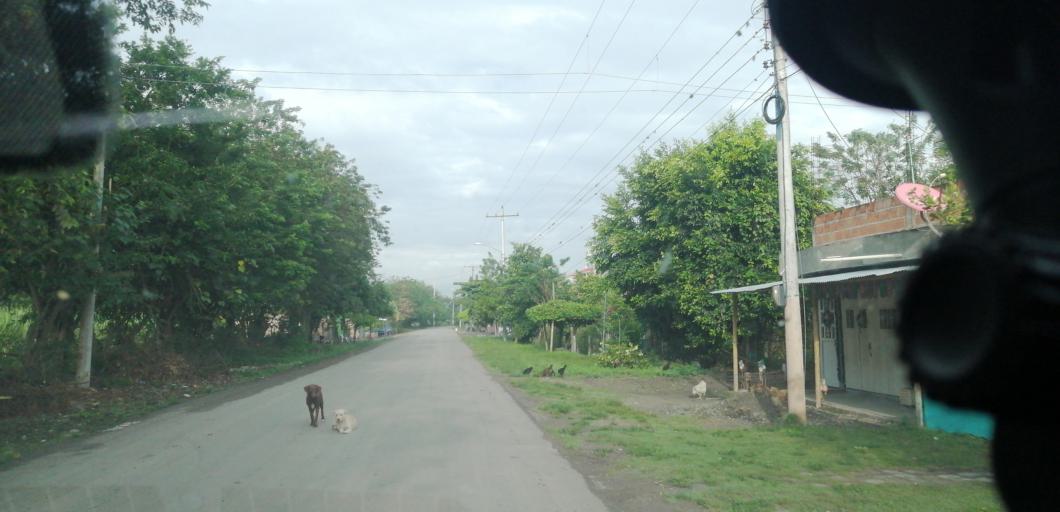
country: CO
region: Valle del Cauca
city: Palmira
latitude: 3.5372
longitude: -76.3576
